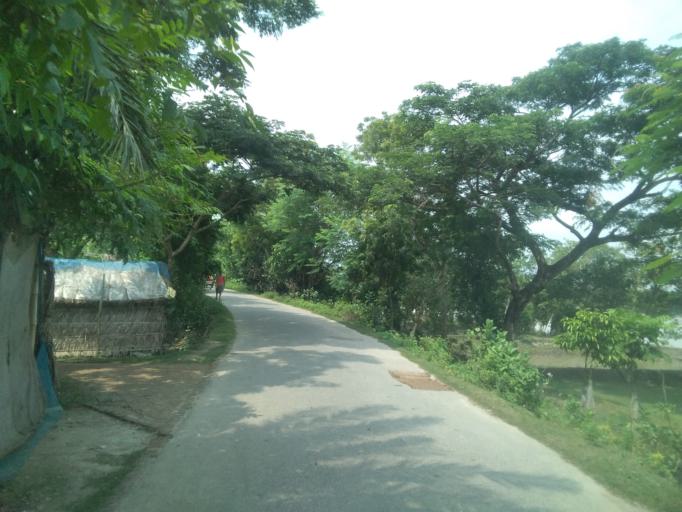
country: BD
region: Khulna
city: Phultala
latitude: 22.7015
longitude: 89.4550
